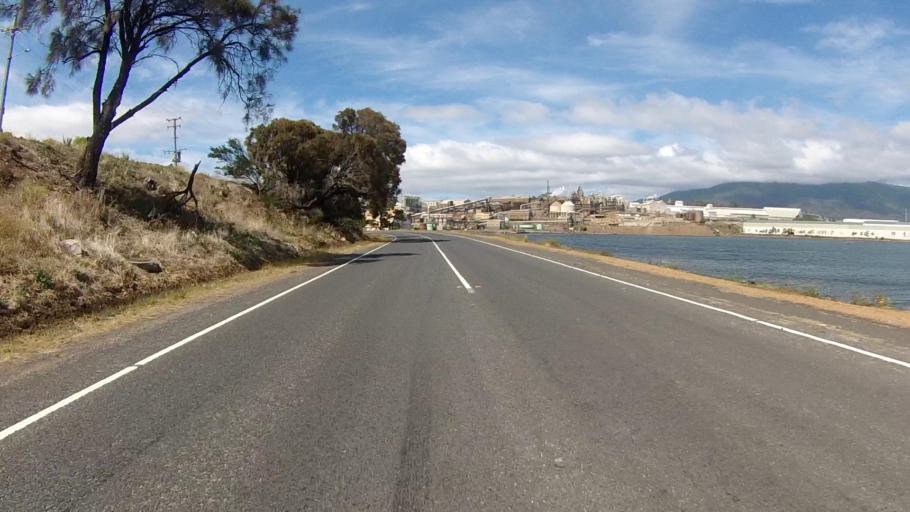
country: AU
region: Tasmania
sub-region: Glenorchy
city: Lutana
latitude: -42.8231
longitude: 147.3176
